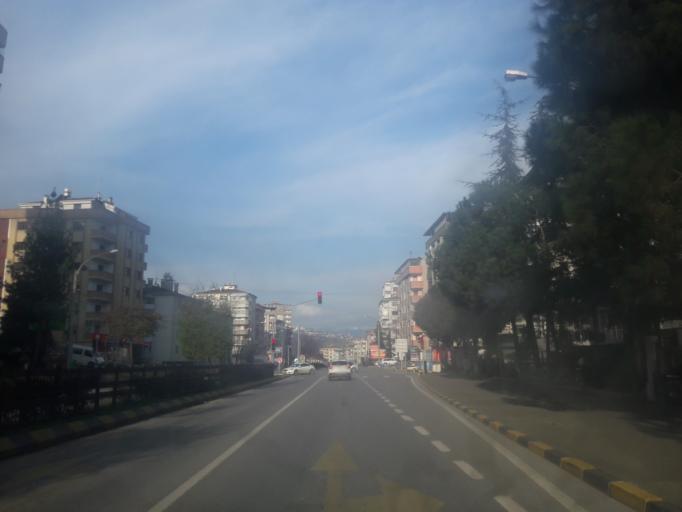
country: TR
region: Trabzon
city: Trabzon
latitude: 40.9968
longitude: 39.6836
